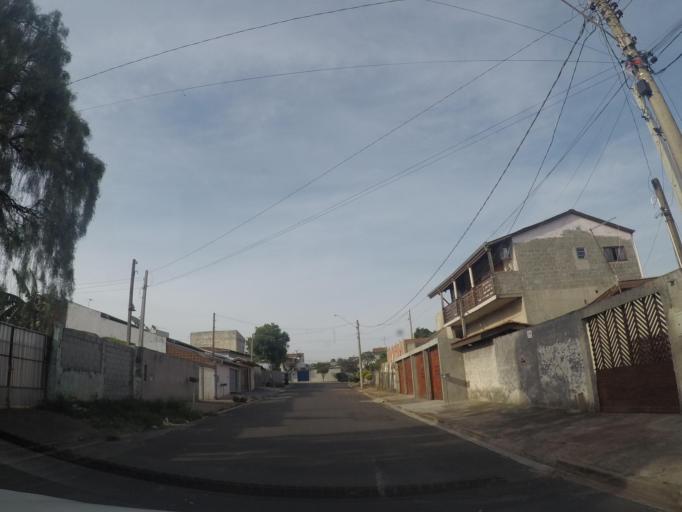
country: BR
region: Sao Paulo
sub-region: Hortolandia
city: Hortolandia
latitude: -22.8274
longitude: -47.1896
